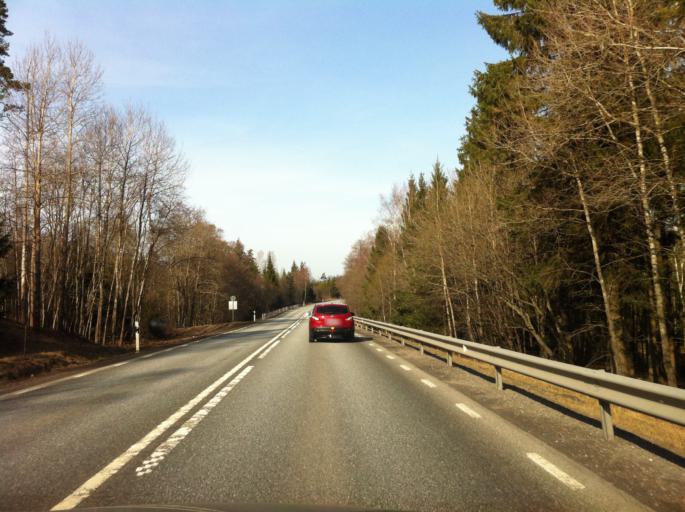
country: SE
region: Joenkoeping
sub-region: Mullsjo Kommun
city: Mullsjoe
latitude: 58.0138
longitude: 13.8291
